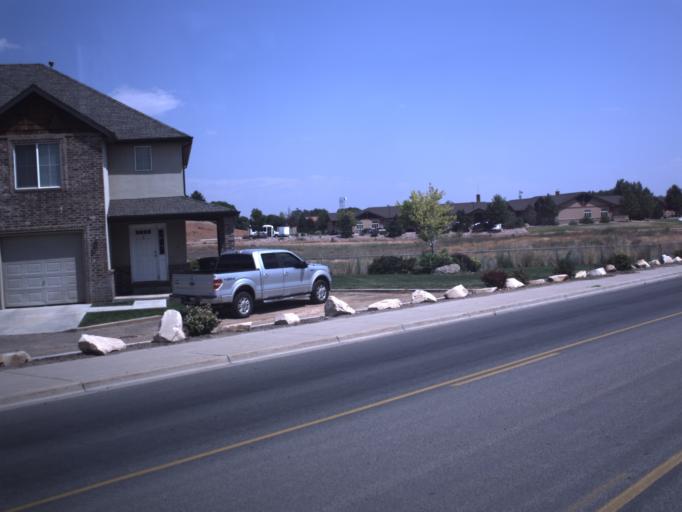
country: US
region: Utah
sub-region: Duchesne County
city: Roosevelt
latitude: 40.3037
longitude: -110.0013
